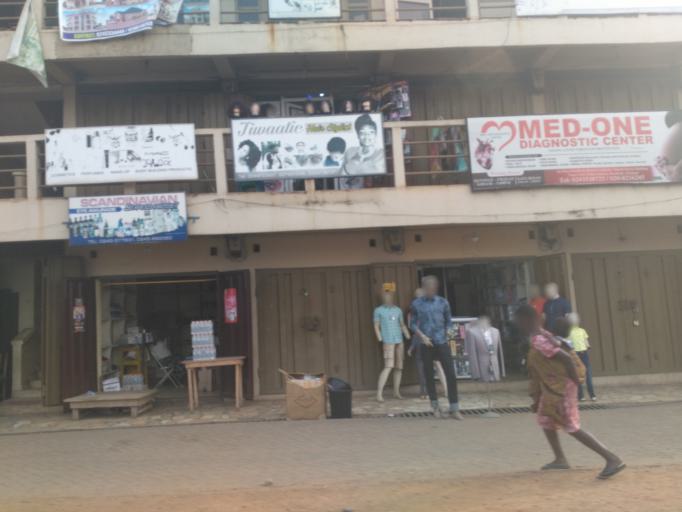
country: GH
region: Ashanti
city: Tafo
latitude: 6.7135
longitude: -1.6175
